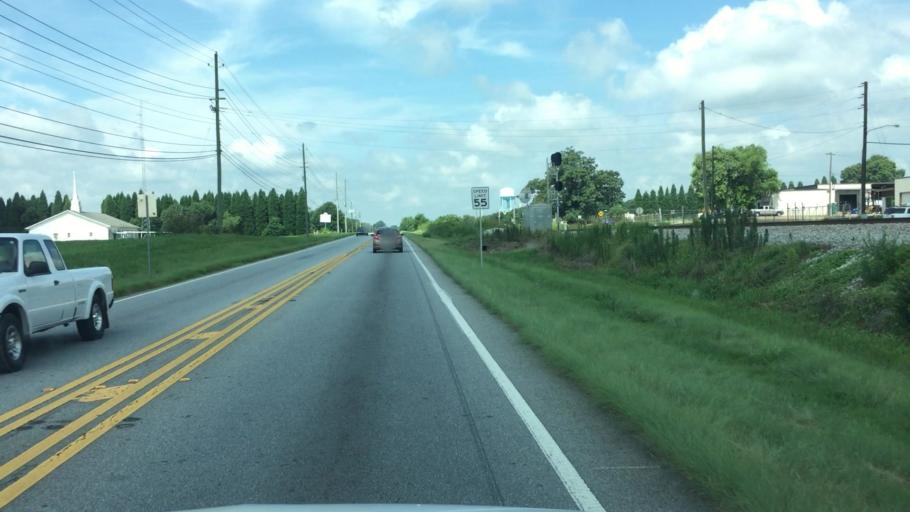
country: US
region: Georgia
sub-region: Barrow County
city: Winder
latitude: 33.9922
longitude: -83.7602
